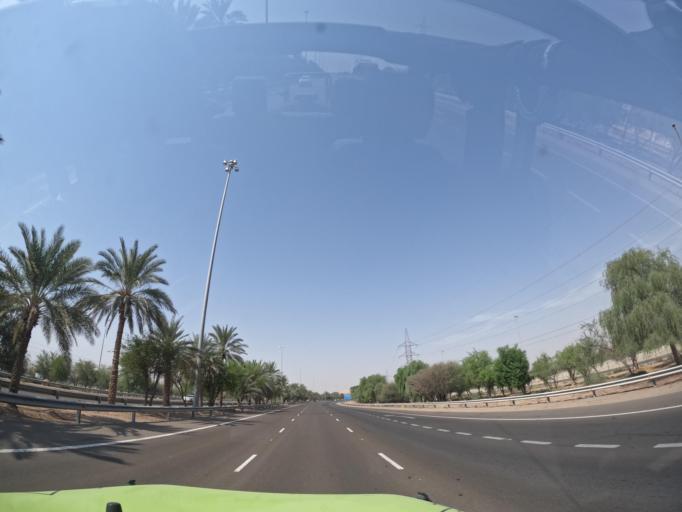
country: AE
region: Abu Dhabi
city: Al Ain
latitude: 24.2110
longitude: 55.5167
